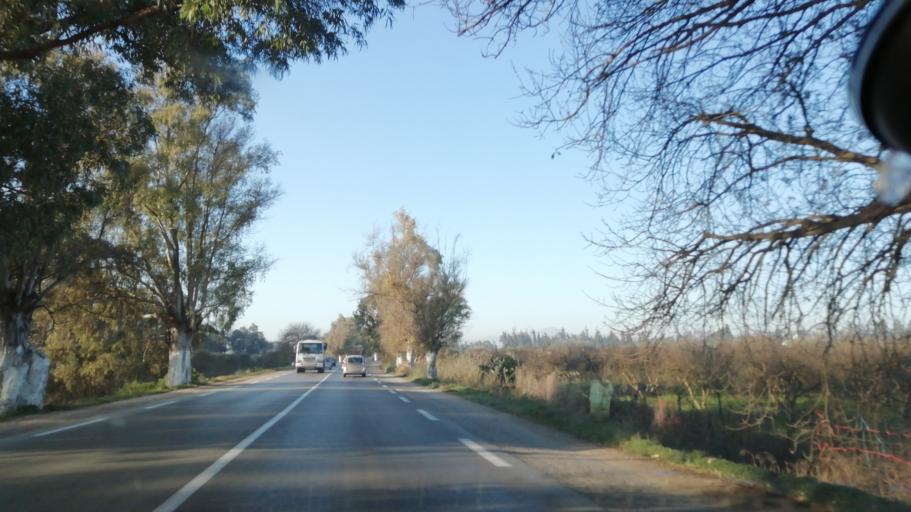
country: DZ
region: Tlemcen
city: Remchi
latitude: 35.0733
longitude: -1.4565
